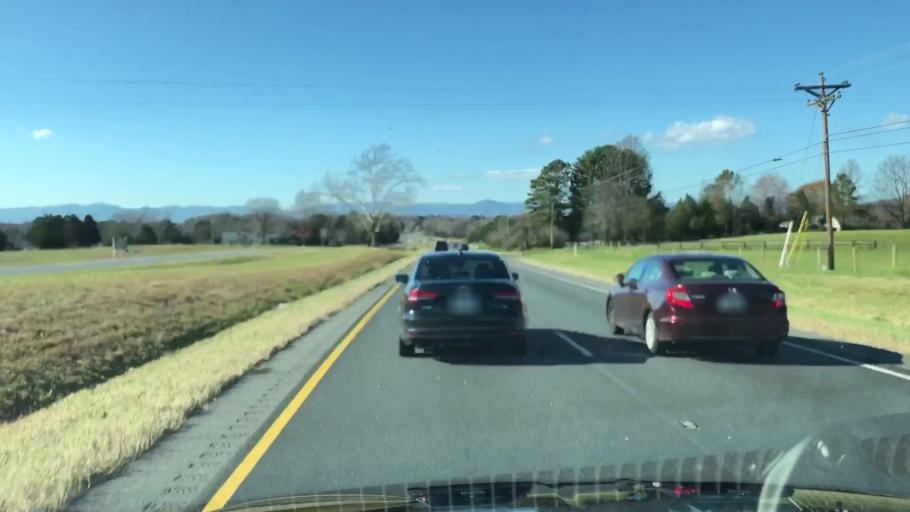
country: US
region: Virginia
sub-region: Culpeper County
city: Merrimac
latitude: 38.4514
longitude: -78.1008
